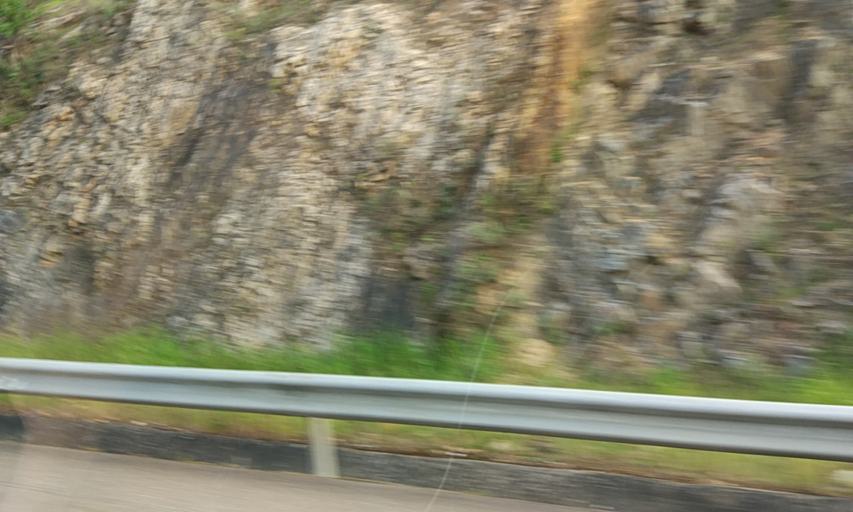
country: PT
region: Portalegre
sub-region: Elvas
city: Elvas
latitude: 38.9025
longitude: -7.1429
